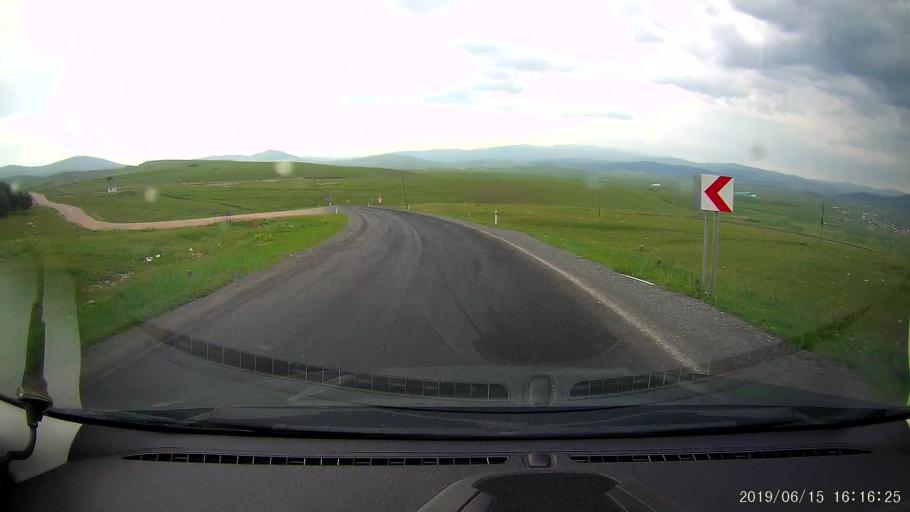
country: TR
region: Ardahan
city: Hanak
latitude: 41.2590
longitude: 42.8526
